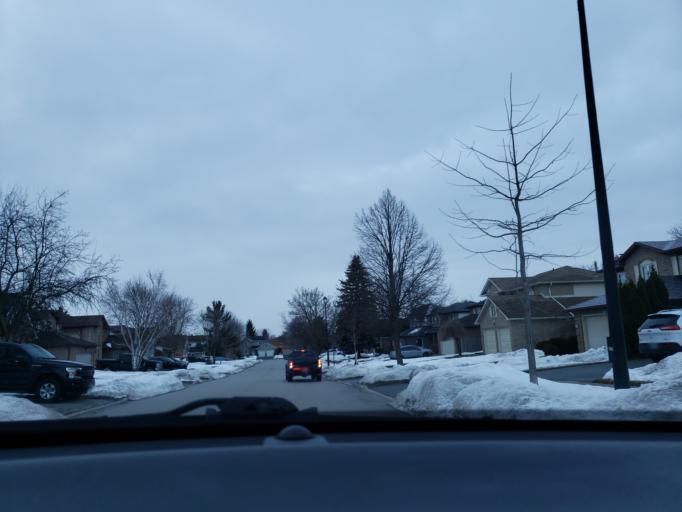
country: CA
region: Ontario
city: Newmarket
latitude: 44.0640
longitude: -79.4685
